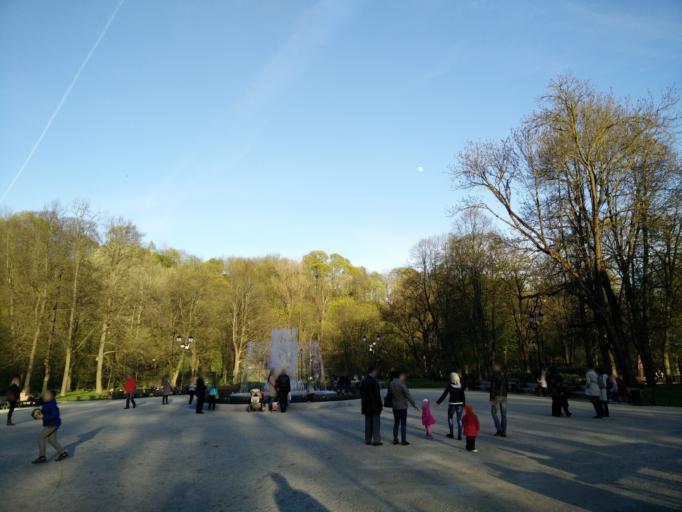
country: LT
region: Vilnius County
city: Rasos
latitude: 54.6839
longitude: 25.2969
